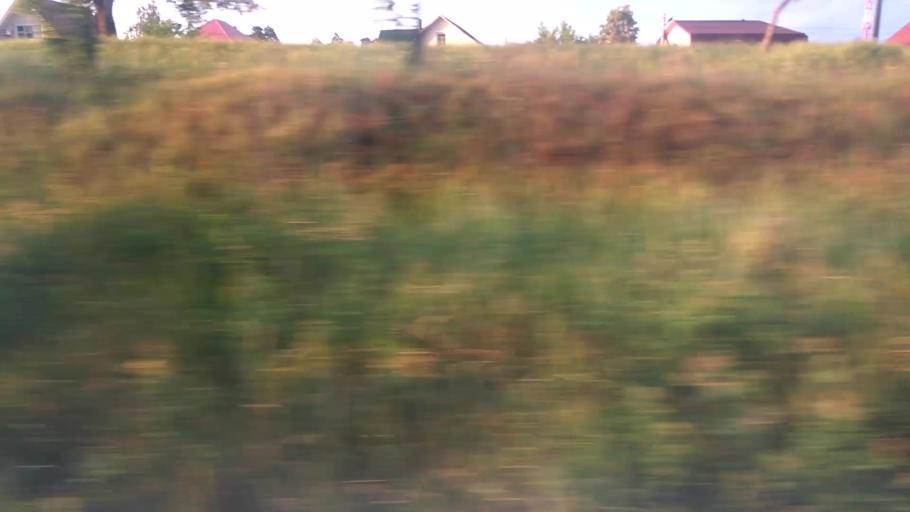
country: RU
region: Moskovskaya
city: Kashira
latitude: 54.8702
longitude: 38.1245
